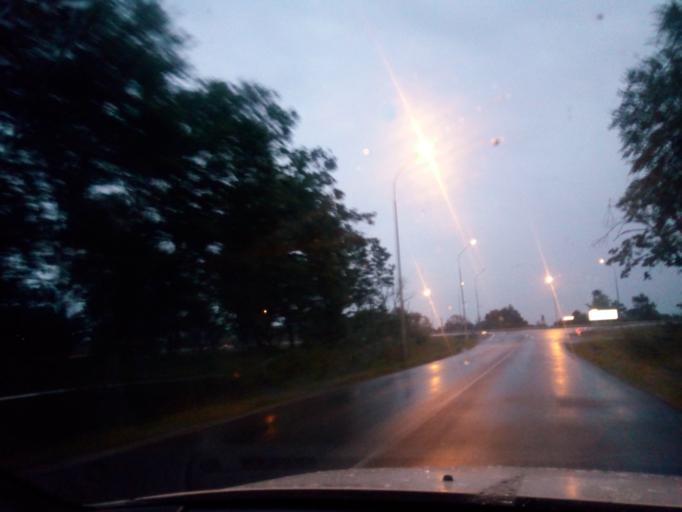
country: RU
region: Primorskiy
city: Dal'nerechensk
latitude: 45.8702
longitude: 133.7214
